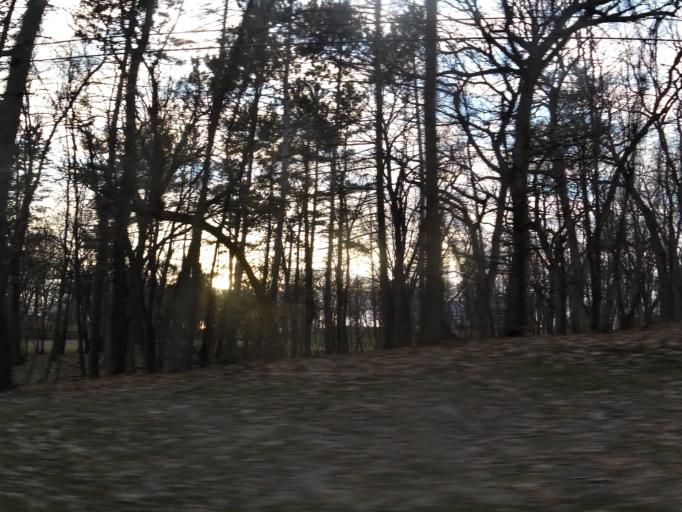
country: US
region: Minnesota
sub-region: Washington County
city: Dellwood
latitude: 45.0795
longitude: -92.9624
